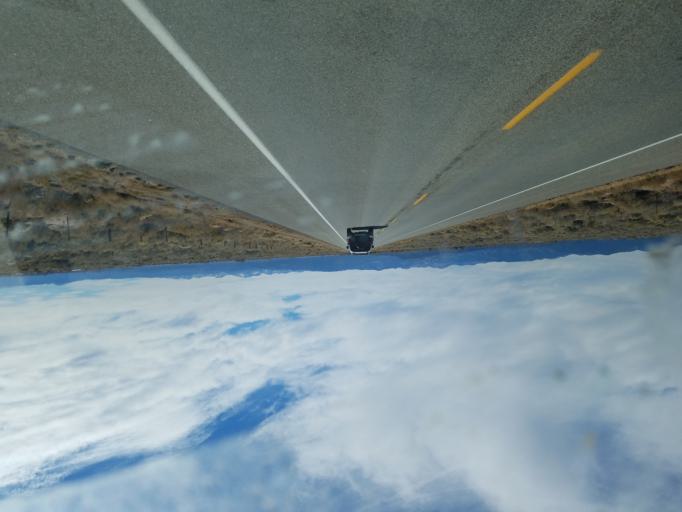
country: US
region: Colorado
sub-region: Costilla County
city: San Luis
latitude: 37.4481
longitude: -105.5393
